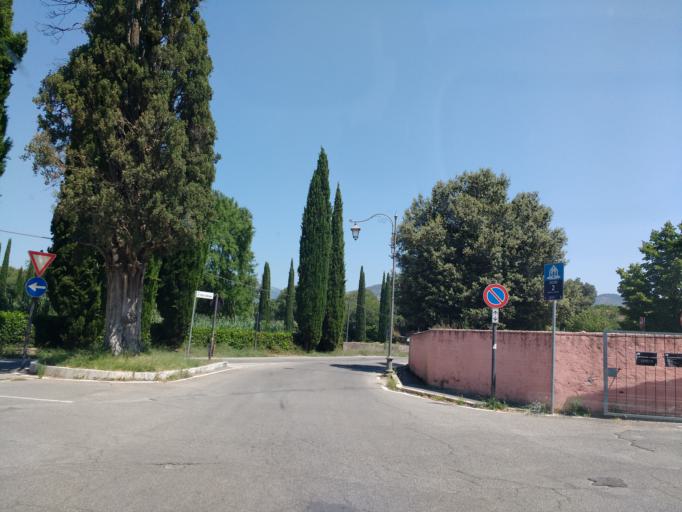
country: IT
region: Latium
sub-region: Citta metropolitana di Roma Capitale
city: Villa Adriana
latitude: 41.9463
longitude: 12.7727
